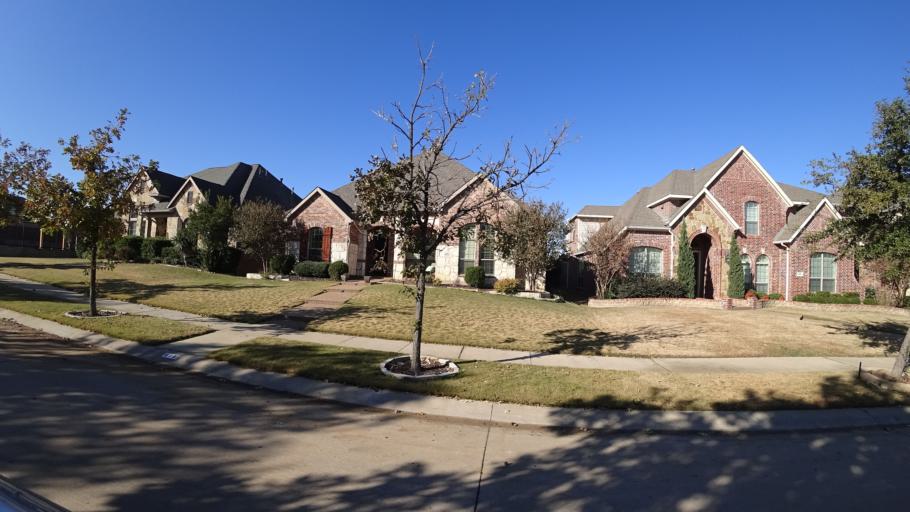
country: US
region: Texas
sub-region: Denton County
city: The Colony
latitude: 33.0418
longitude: -96.9177
